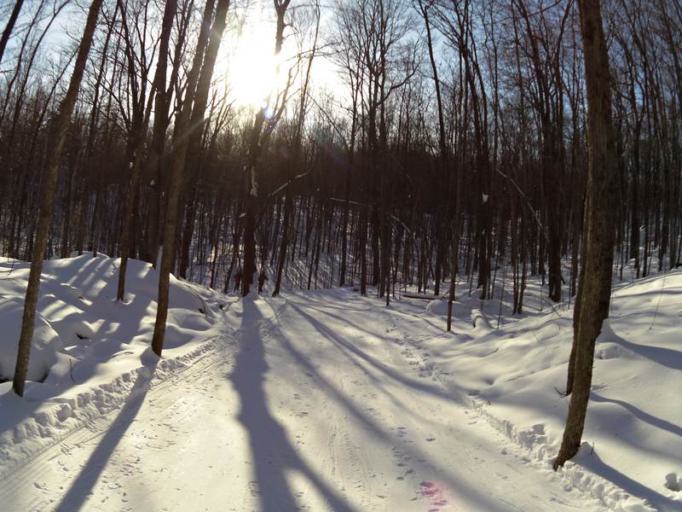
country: CA
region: Quebec
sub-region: Outaouais
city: Gatineau
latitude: 45.4741
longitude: -75.7947
